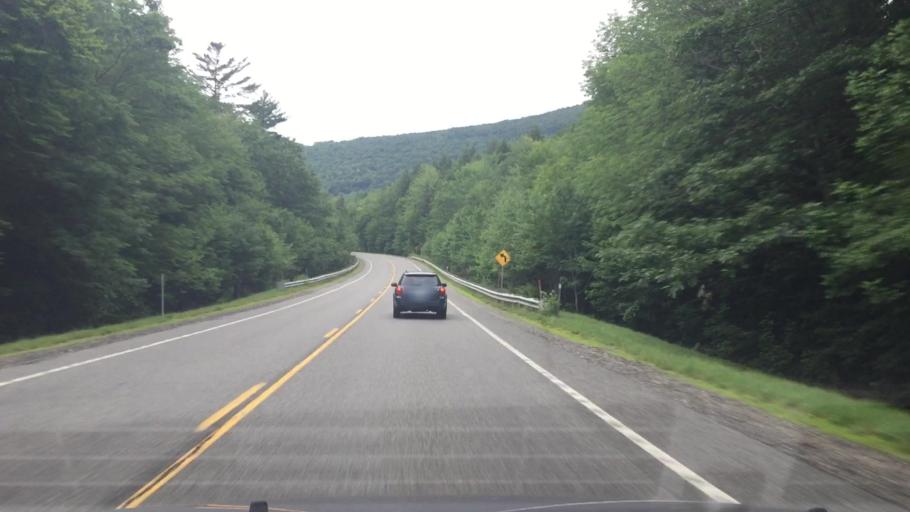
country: US
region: New Hampshire
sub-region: Carroll County
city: North Conway
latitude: 44.0904
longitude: -71.3536
